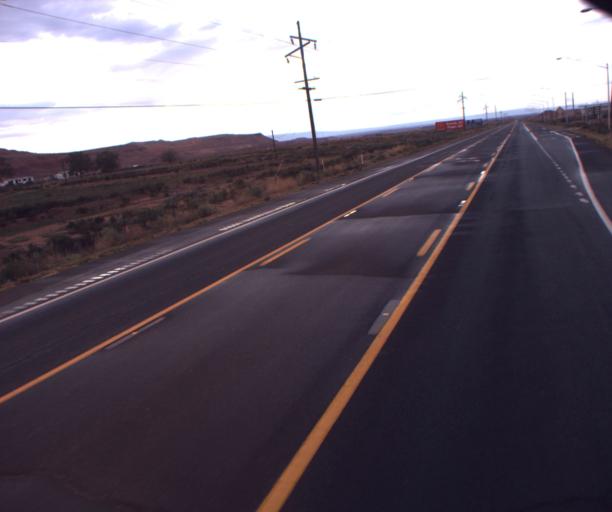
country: US
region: Arizona
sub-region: Coconino County
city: Tuba City
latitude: 36.1077
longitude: -111.2472
